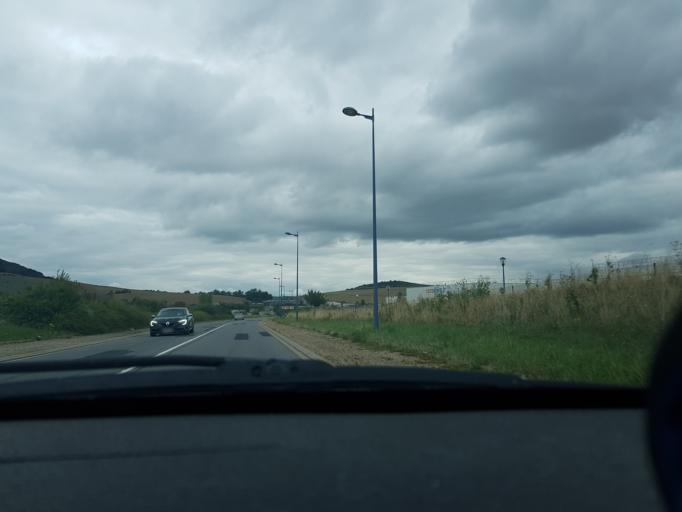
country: FR
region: Lorraine
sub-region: Departement de Meurthe-et-Moselle
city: Saulxures-les-Nancy
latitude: 48.7026
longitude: 6.2423
